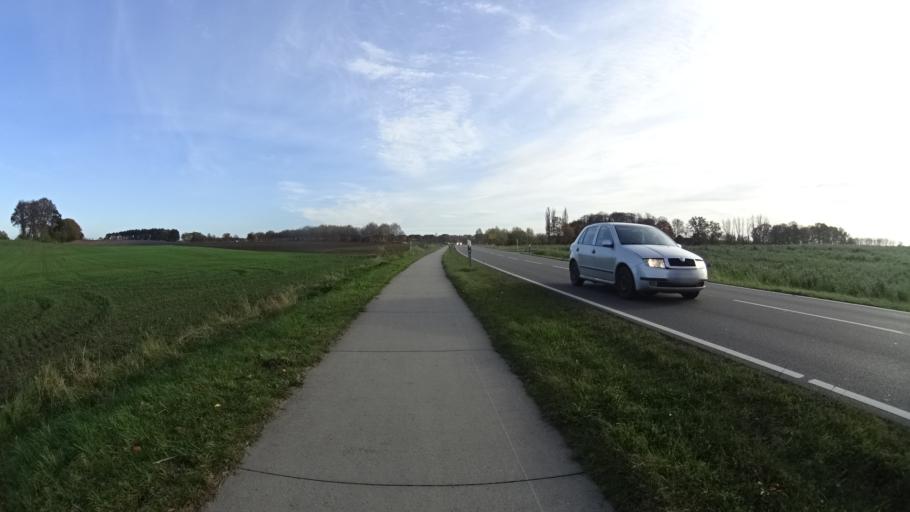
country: DE
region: Lower Saxony
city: Wendisch Evern
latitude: 53.2227
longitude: 10.4602
